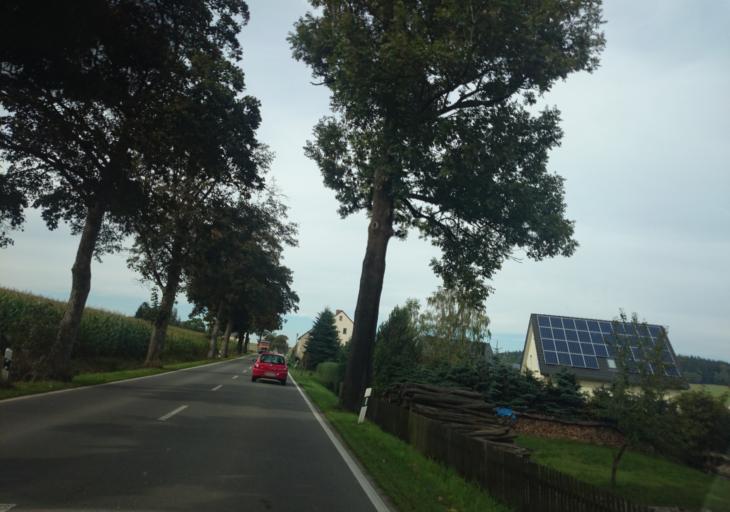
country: DE
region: Saxony
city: Bornichen
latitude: 50.7496
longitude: 13.1356
